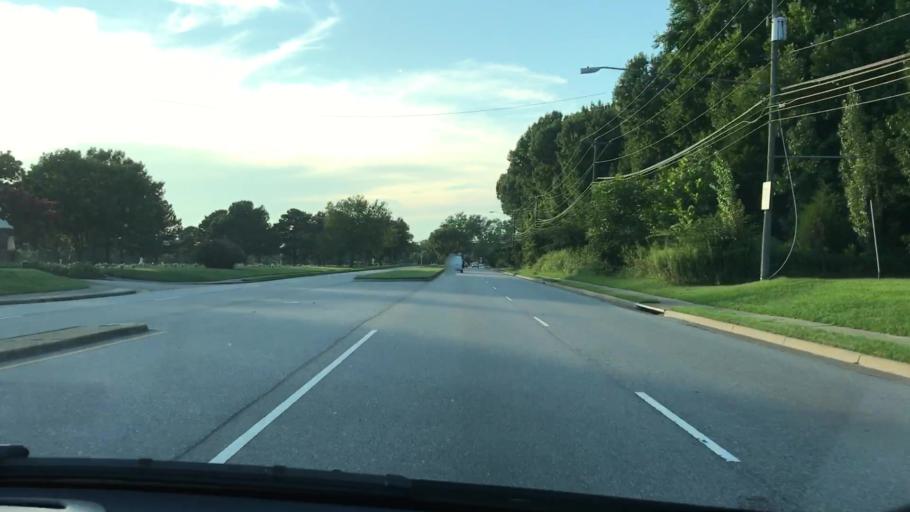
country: US
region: Virginia
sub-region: City of Hampton
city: Hampton
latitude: 37.0560
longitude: -76.3822
